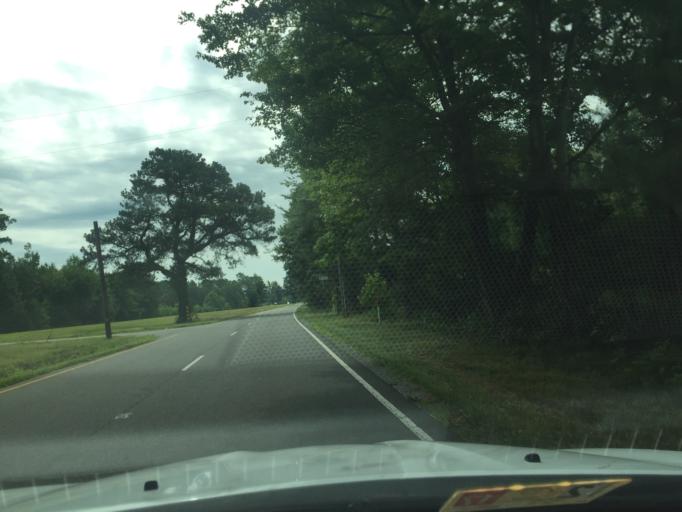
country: US
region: Virginia
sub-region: Charles City County
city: Charles City
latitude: 37.4474
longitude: -77.0648
